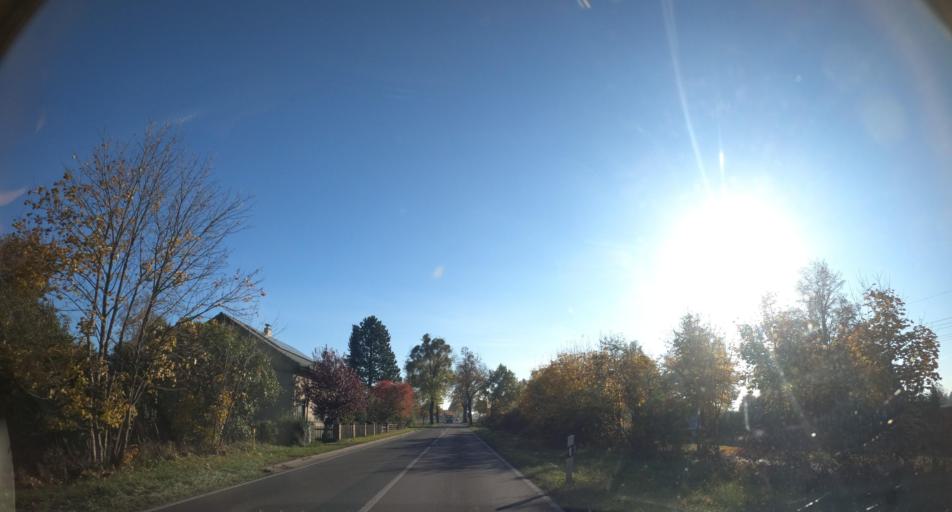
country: DE
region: Mecklenburg-Vorpommern
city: Ueckermunde
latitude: 53.7233
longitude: 14.0617
